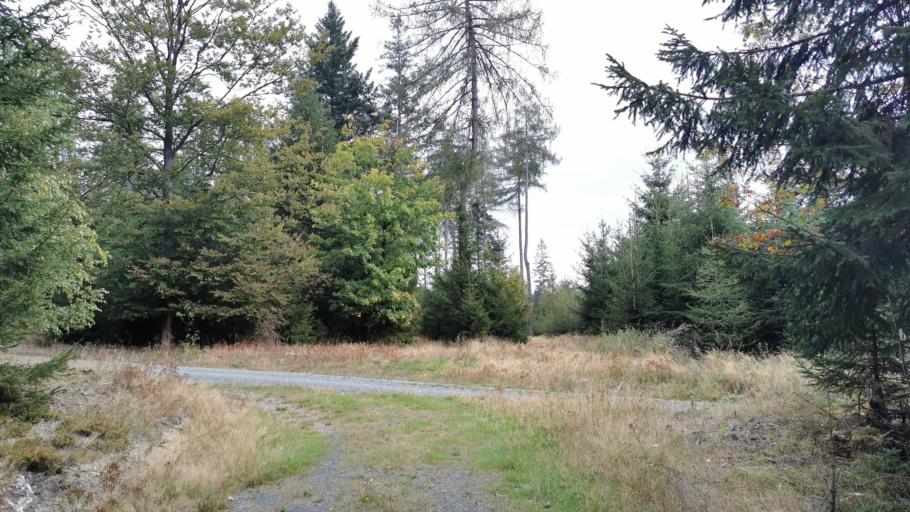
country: DE
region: Bavaria
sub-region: Upper Franconia
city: Steinwiesen
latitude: 50.3415
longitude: 11.4556
